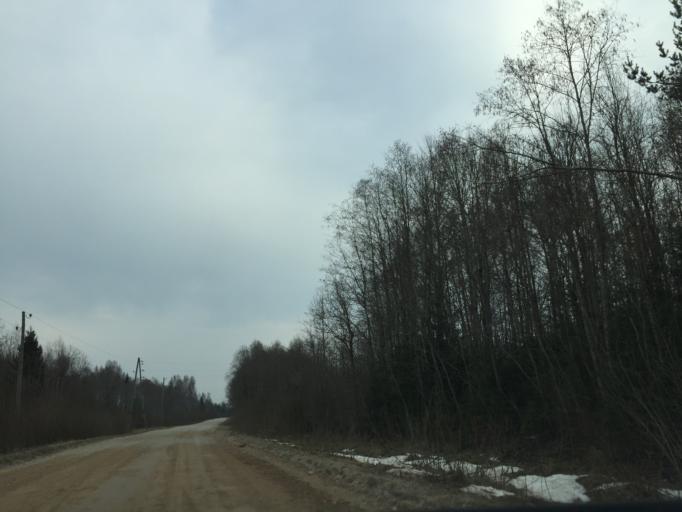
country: LV
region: Priekuli
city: Priekuli
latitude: 57.1763
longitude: 25.4847
